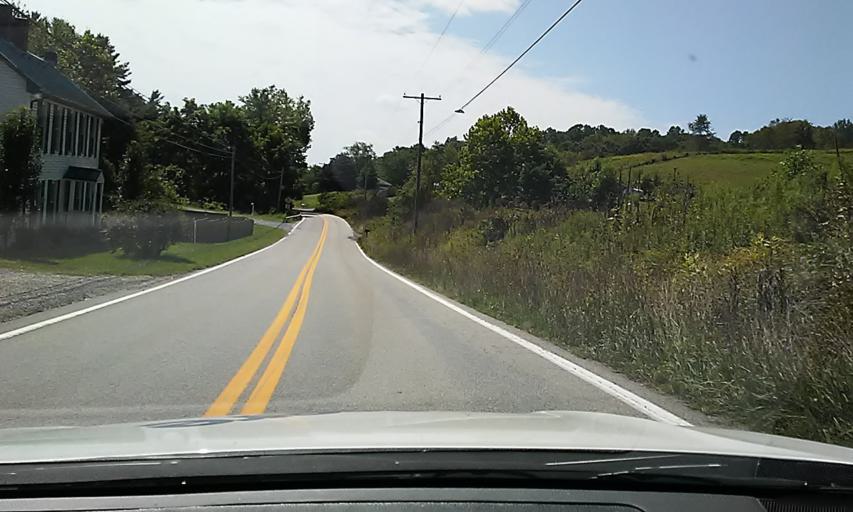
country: US
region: West Virginia
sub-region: Monongalia County
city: Star City
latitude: 39.6129
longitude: -80.0601
